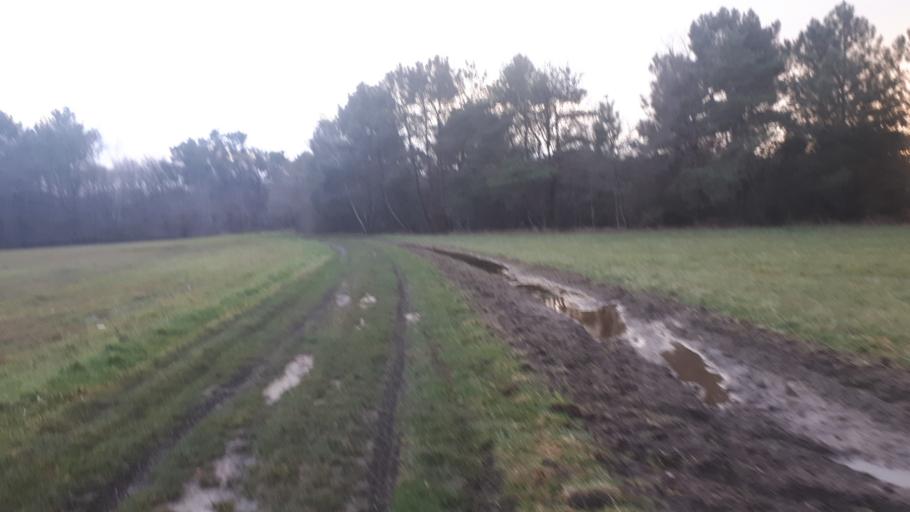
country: FR
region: Centre
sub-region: Departement du Loir-et-Cher
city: Saint-Romain-sur-Cher
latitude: 47.3463
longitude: 1.3952
